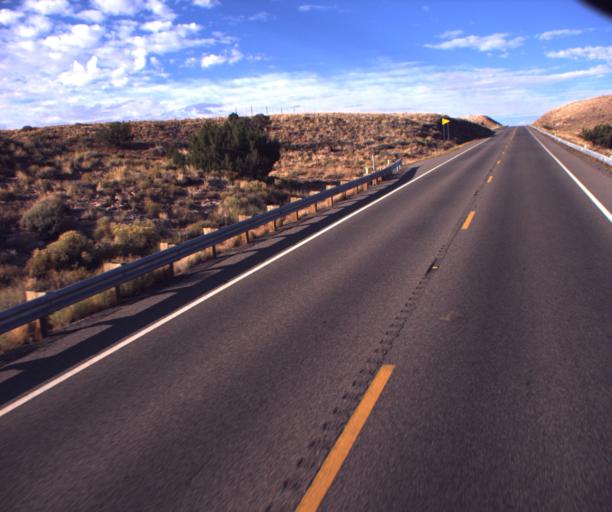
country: US
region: New Mexico
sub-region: San Juan County
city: Shiprock
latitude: 36.9296
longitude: -109.1568
